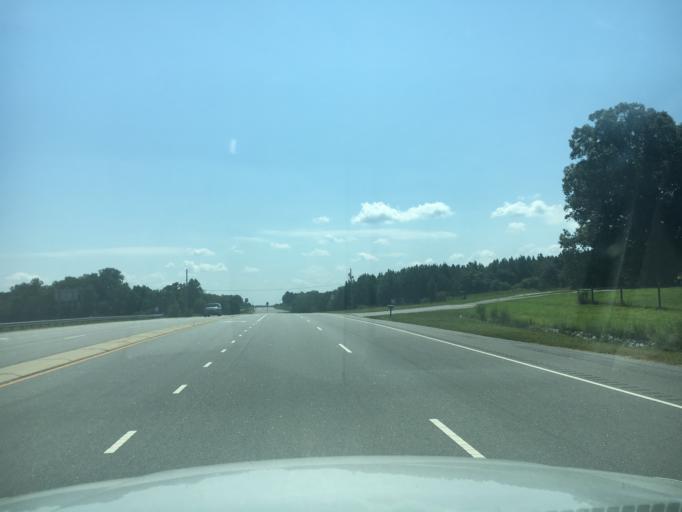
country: US
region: North Carolina
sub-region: Rutherford County
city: Spindale
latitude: 35.3060
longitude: -81.9213
